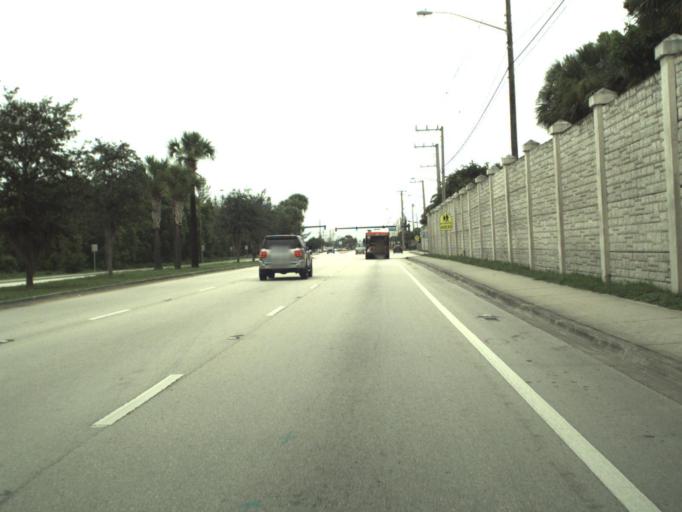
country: US
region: Florida
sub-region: Palm Beach County
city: Mangonia Park
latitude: 26.7525
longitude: -80.1089
